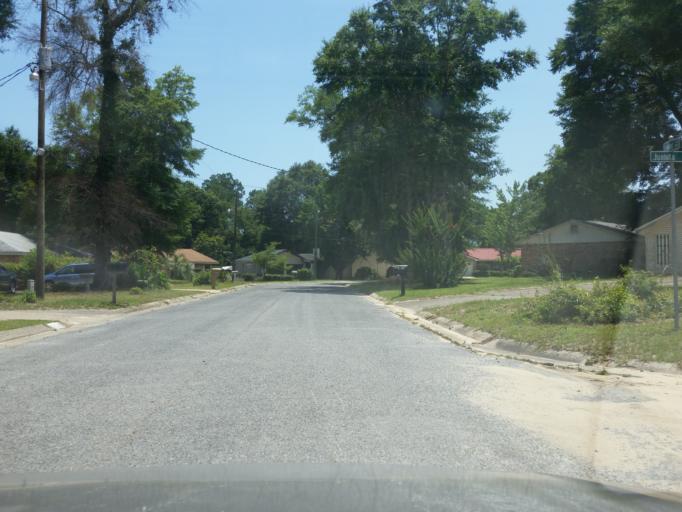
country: US
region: Florida
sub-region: Escambia County
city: Ferry Pass
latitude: 30.5145
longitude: -87.1908
